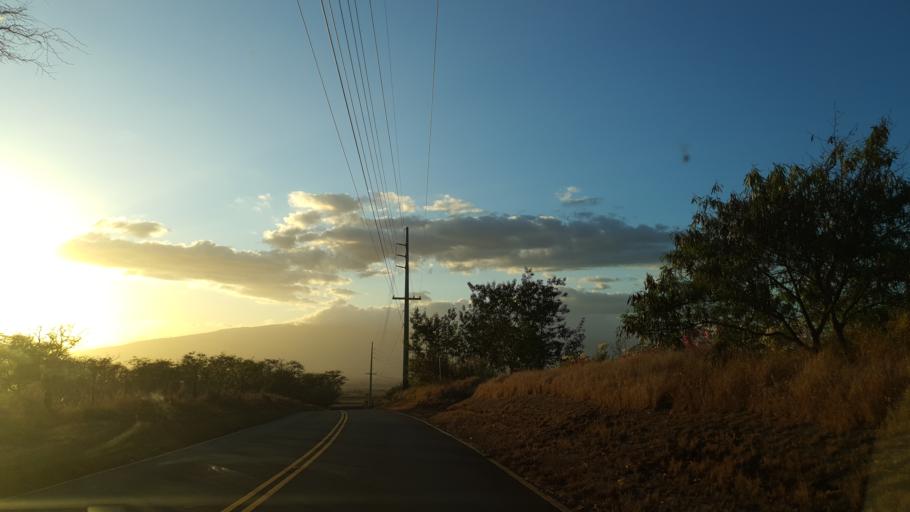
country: US
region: Hawaii
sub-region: Maui County
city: Pukalani
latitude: 20.7954
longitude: -156.3675
